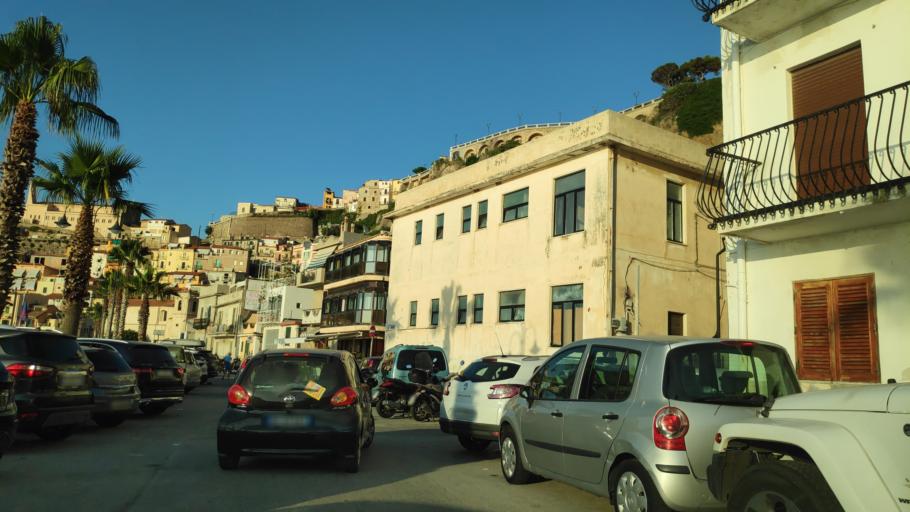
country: IT
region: Calabria
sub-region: Provincia di Reggio Calabria
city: Scilla
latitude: 38.2534
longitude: 15.7132
